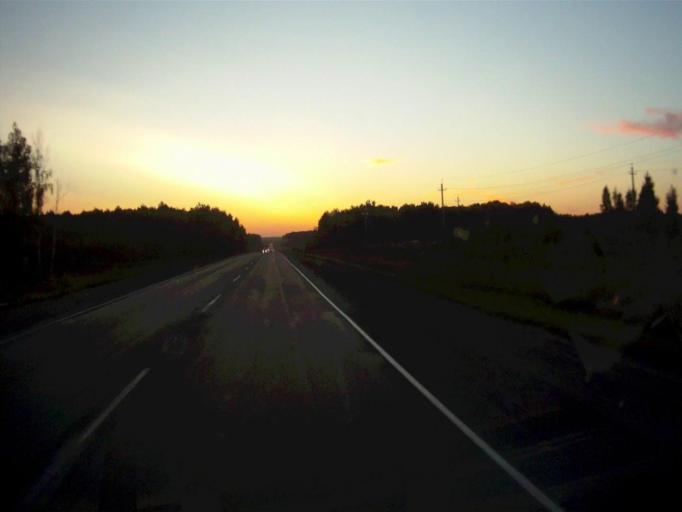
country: RU
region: Chelyabinsk
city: Poletayevo
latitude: 55.2174
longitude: 61.0418
